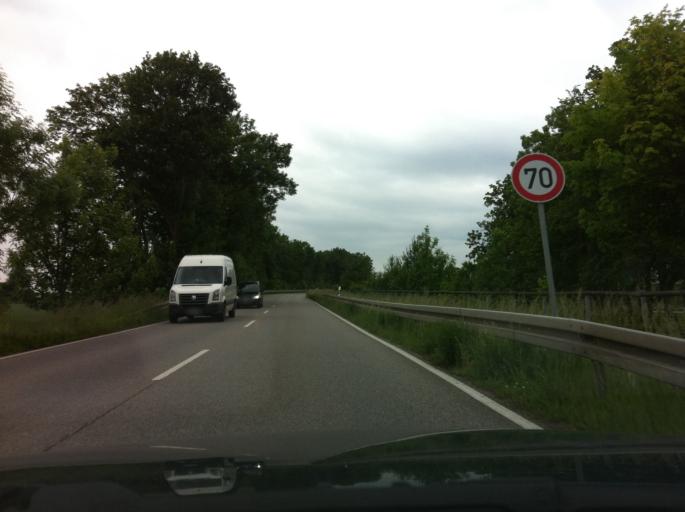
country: DE
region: Bavaria
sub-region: Upper Bavaria
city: Unterhaching
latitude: 48.0793
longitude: 11.6223
